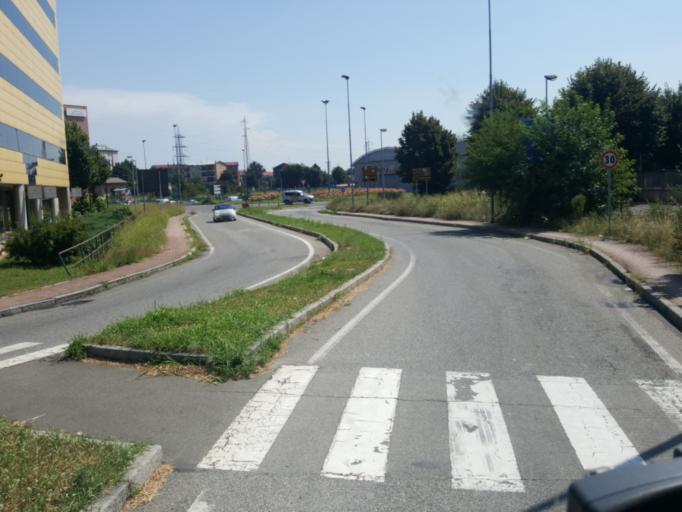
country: IT
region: Lombardy
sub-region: Citta metropolitana di Milano
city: Sesto San Giovanni
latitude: 45.5552
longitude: 9.2491
